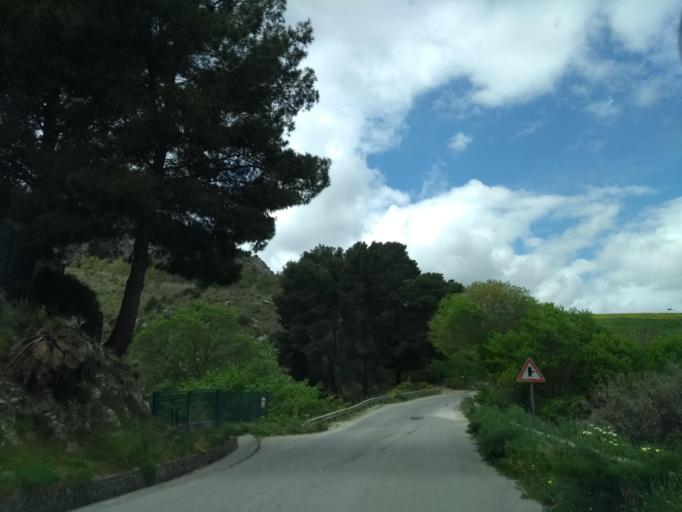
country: IT
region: Sicily
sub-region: Trapani
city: Calatafimi
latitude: 37.9445
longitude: 12.8332
